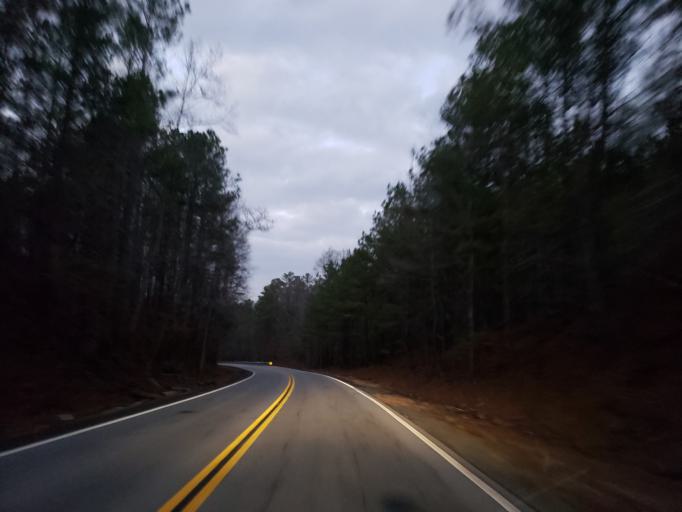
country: US
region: Georgia
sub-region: Carroll County
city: Temple
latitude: 33.7571
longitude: -85.0406
